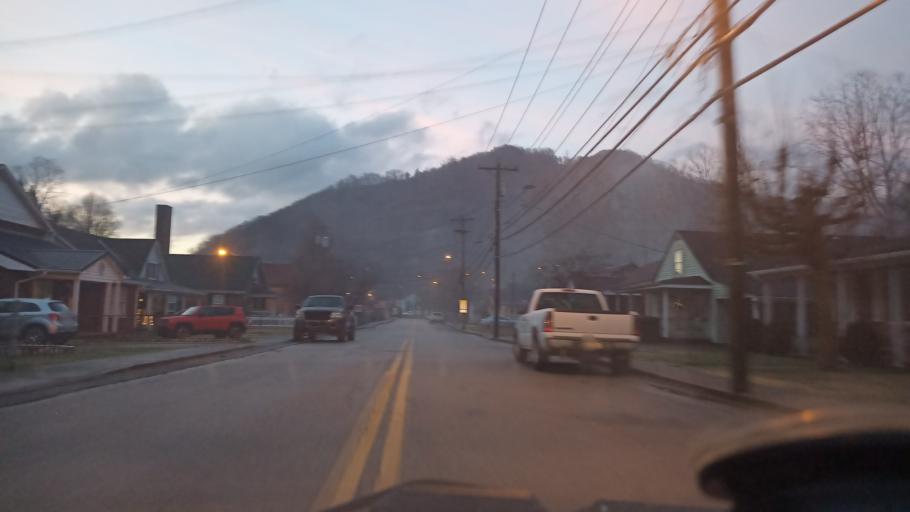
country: US
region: West Virginia
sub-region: Logan County
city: Mallory
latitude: 37.7371
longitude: -81.8759
